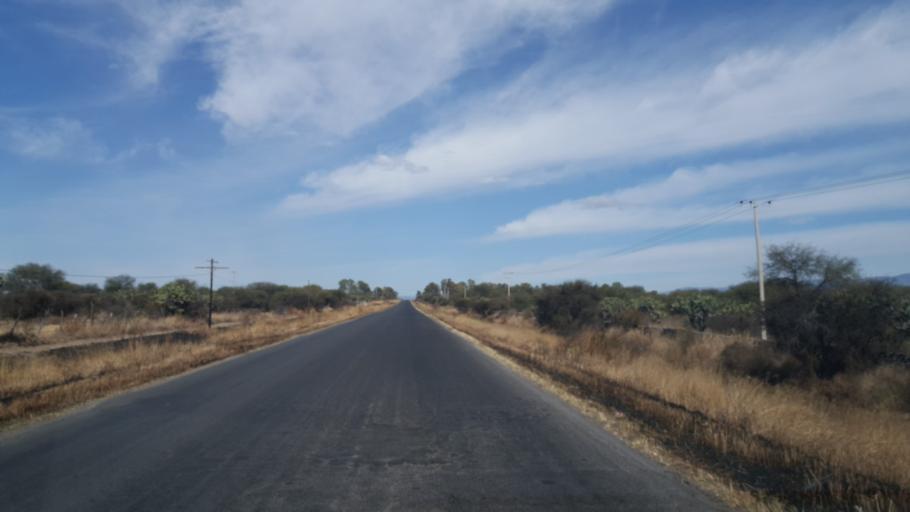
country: MX
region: Jalisco
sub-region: Lagos de Moreno
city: Geovillas Laureles del Campanario
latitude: 21.2833
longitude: -101.9354
